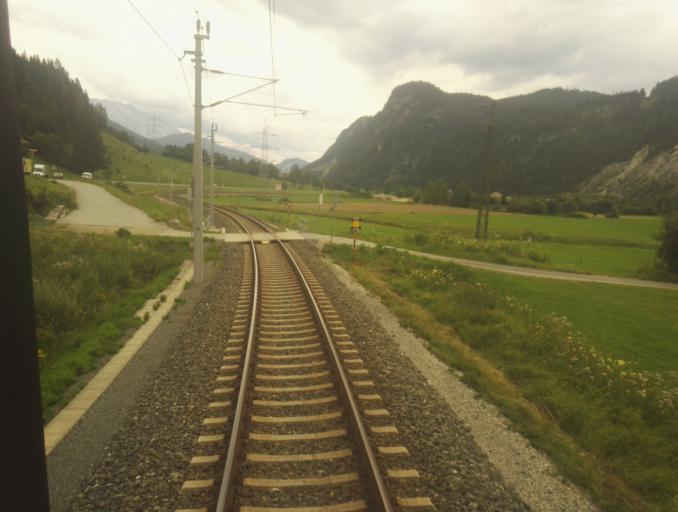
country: AT
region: Salzburg
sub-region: Politischer Bezirk Sankt Johann im Pongau
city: Radstadt
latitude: 47.3867
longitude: 13.4852
